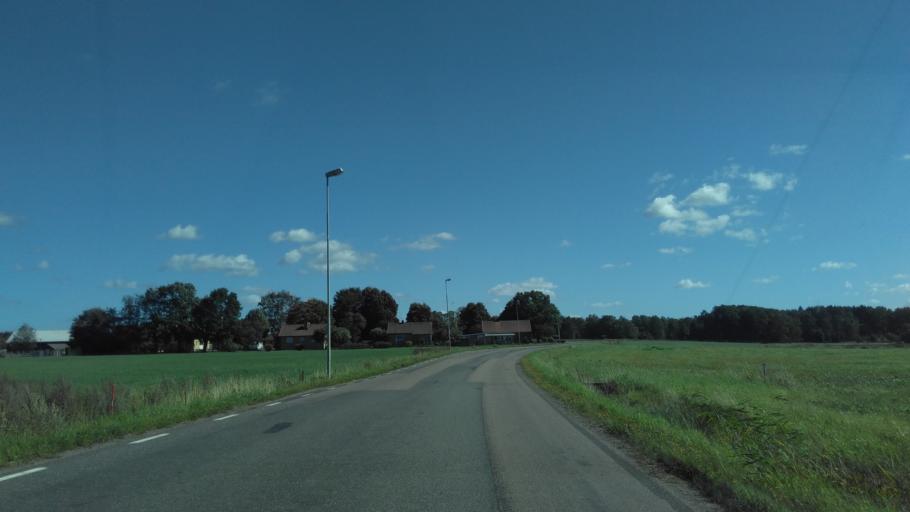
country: SE
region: Vaestra Goetaland
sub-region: Skara Kommun
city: Skara
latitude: 58.3855
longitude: 13.4841
